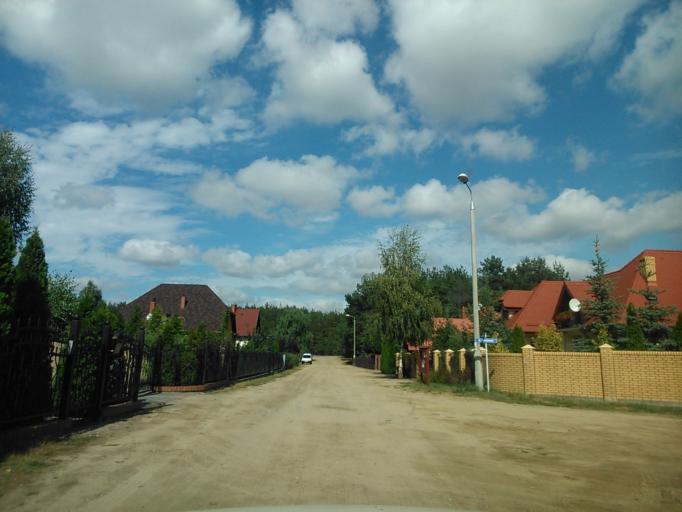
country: PL
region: Kujawsko-Pomorskie
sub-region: Powiat golubsko-dobrzynski
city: Golub-Dobrzyn
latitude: 53.0960
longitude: 19.0442
